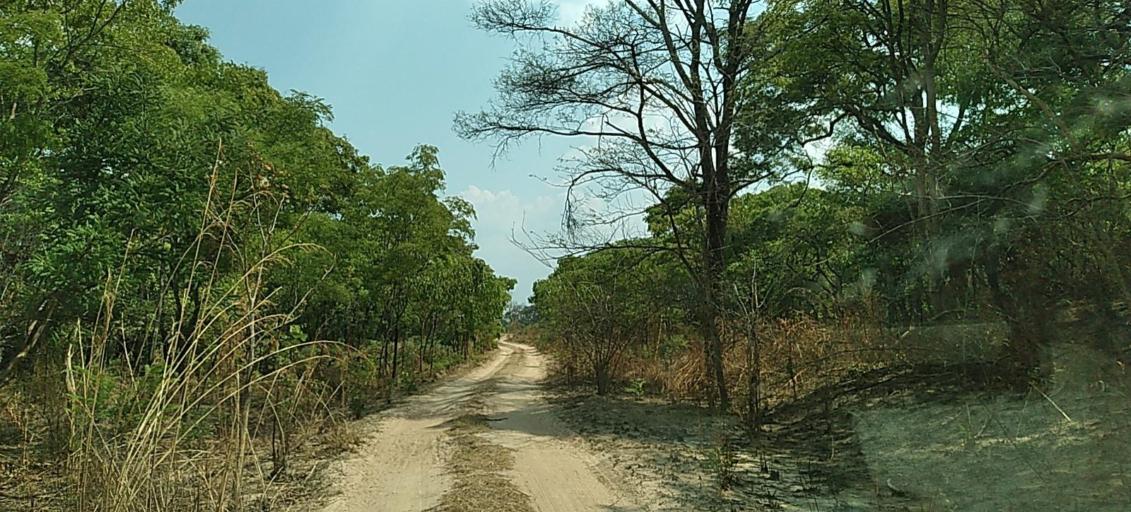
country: ZM
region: Copperbelt
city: Mpongwe
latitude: -13.8694
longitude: 27.9243
